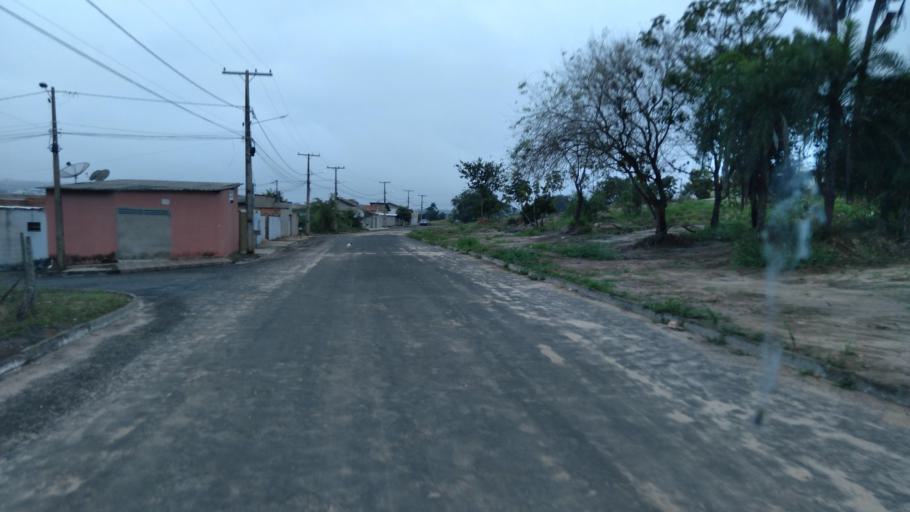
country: BR
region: Goias
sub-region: Mineiros
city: Mineiros
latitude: -17.5733
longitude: -52.5445
